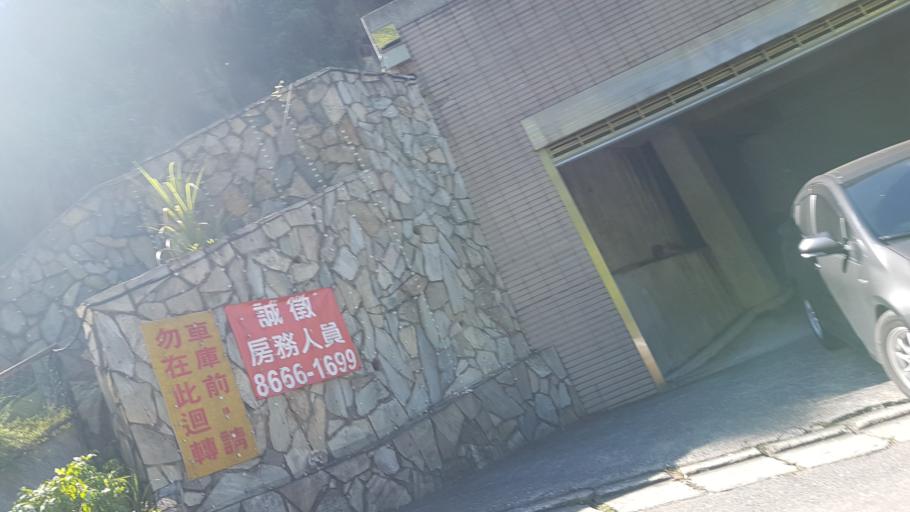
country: TW
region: Taipei
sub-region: Taipei
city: Banqiao
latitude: 24.9535
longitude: 121.5317
